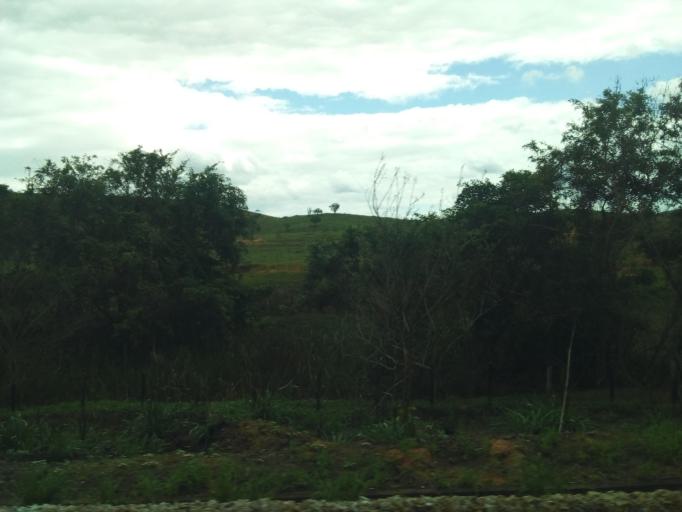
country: BR
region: Minas Gerais
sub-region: Governador Valadares
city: Governador Valadares
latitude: -19.0627
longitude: -42.1489
